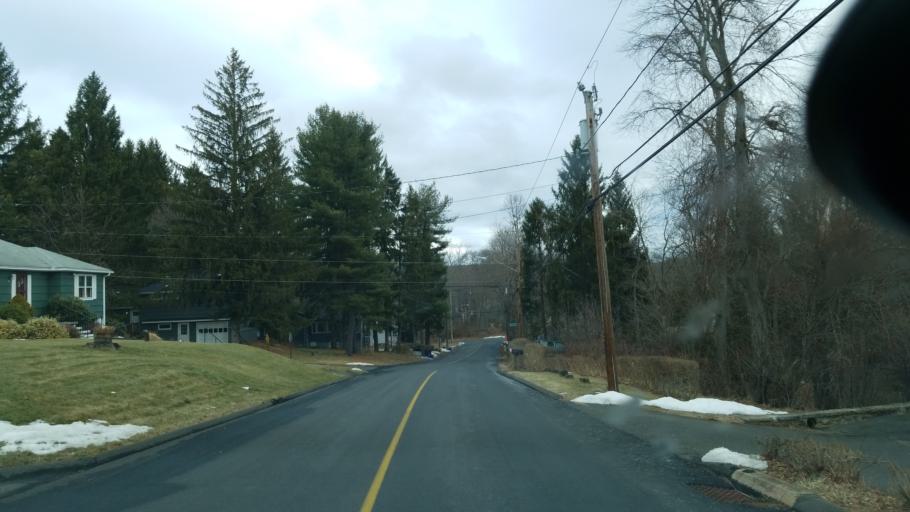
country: US
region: Connecticut
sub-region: New Haven County
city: Wolcott
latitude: 41.5619
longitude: -72.9562
